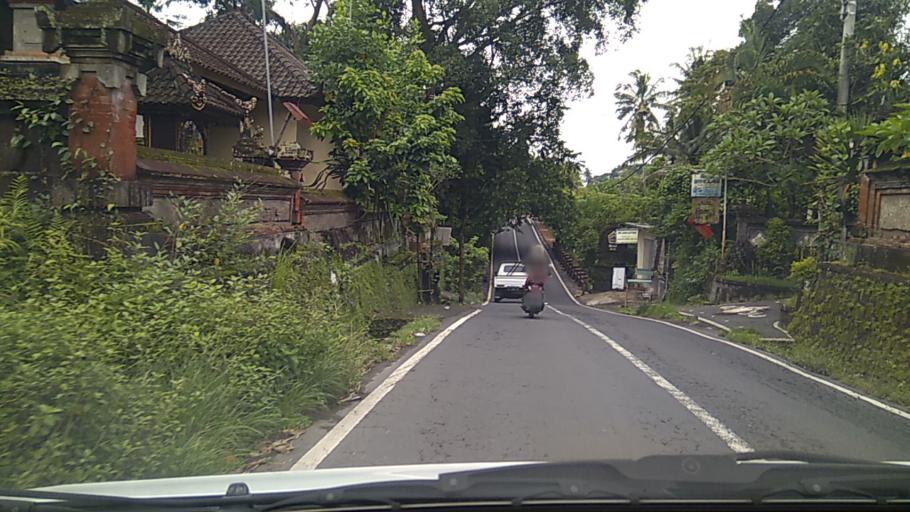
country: ID
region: Bali
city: Banjar Tebongkang
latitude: -8.5286
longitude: 115.2324
